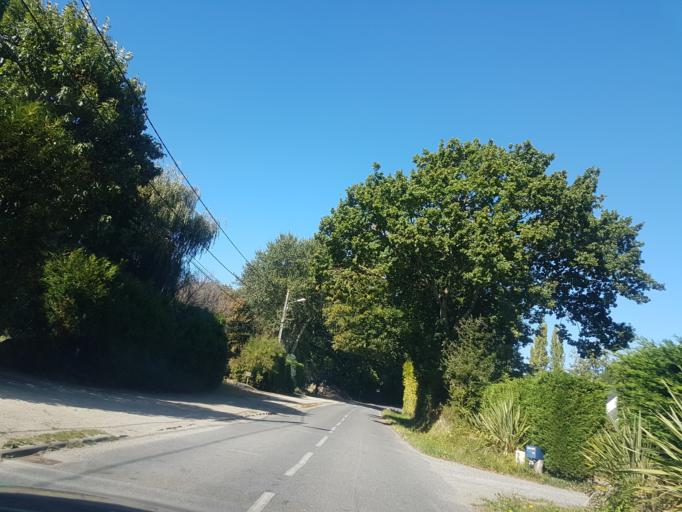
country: FR
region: Pays de la Loire
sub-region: Departement de la Loire-Atlantique
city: Mesquer
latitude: 47.3937
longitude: -2.4494
